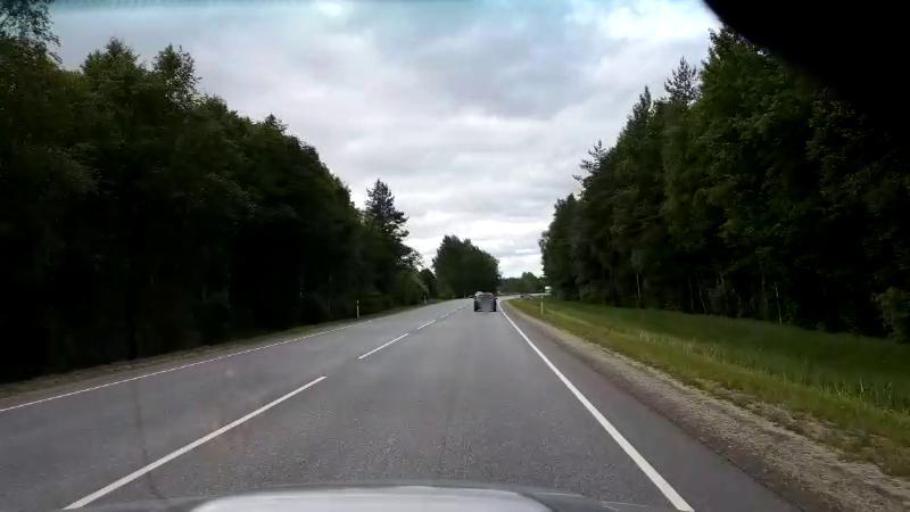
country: EE
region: Raplamaa
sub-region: Maerjamaa vald
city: Marjamaa
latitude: 58.9449
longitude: 24.4675
